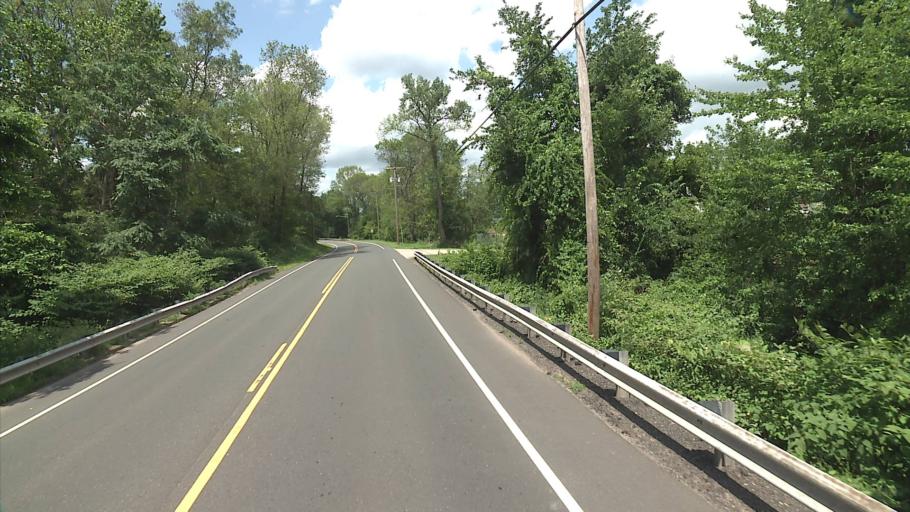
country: US
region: Connecticut
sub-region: Middlesex County
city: Higganum
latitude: 41.4879
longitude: -72.5202
